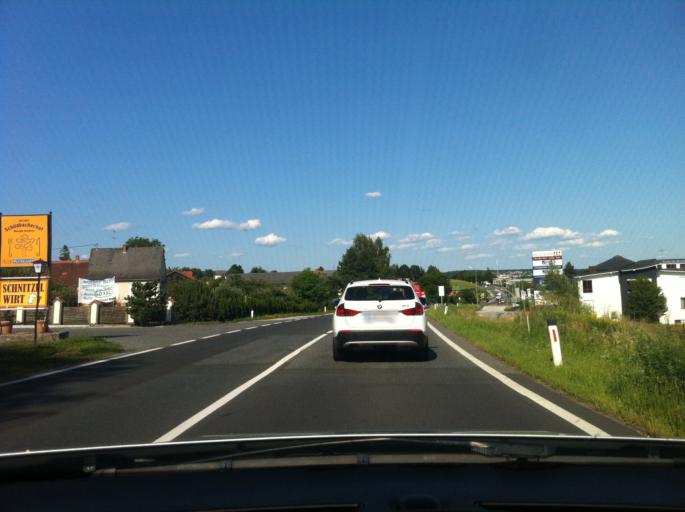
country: AT
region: Styria
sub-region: Politischer Bezirk Hartberg-Fuerstenfeld
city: Hartberg
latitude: 47.2706
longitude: 15.9549
